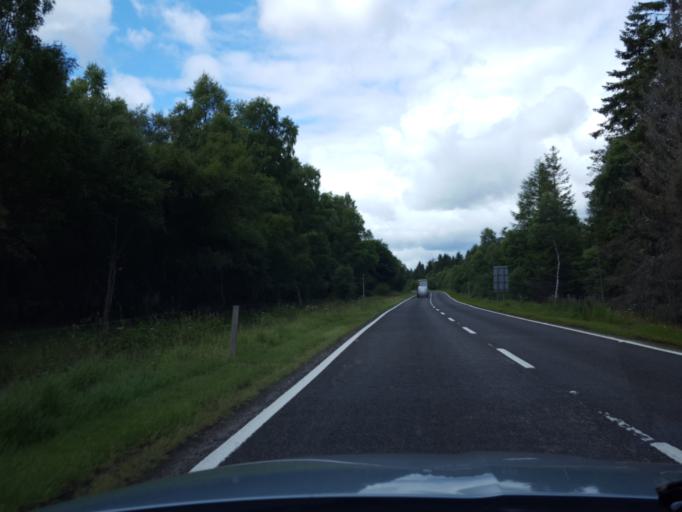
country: GB
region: Scotland
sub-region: Highland
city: Grantown on Spey
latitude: 57.3197
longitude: -3.5798
